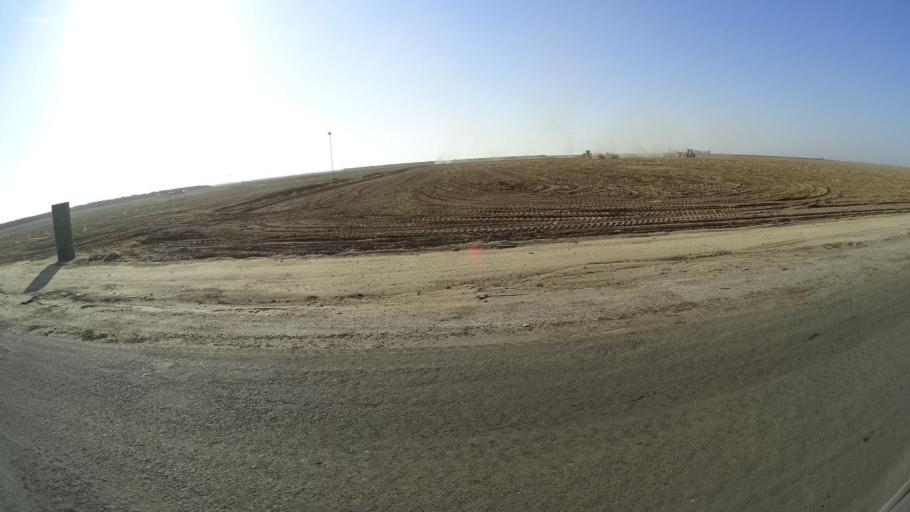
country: US
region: California
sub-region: Tulare County
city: Richgrove
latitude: 35.7688
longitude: -119.1586
